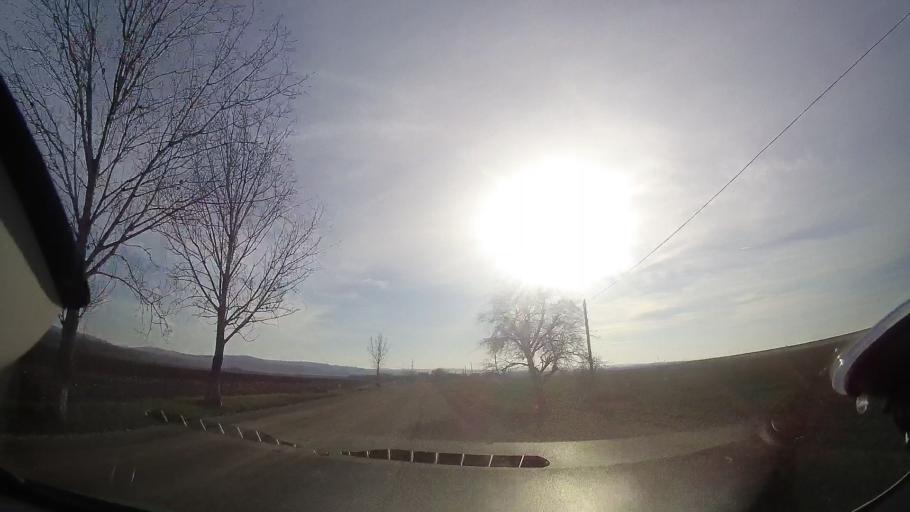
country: RO
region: Bihor
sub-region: Comuna Ciuhoiu
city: Ciuhoiu
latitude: 47.2213
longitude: 22.1345
